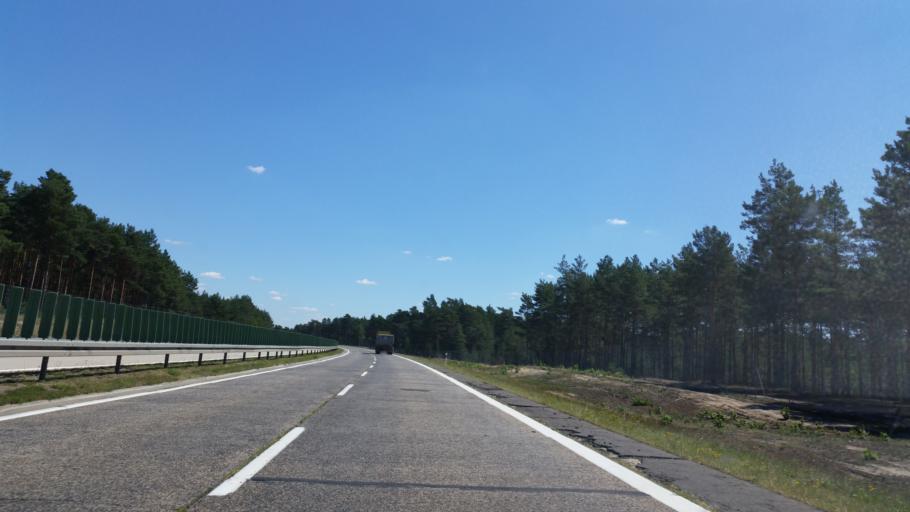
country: PL
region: Lubusz
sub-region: Powiat zaganski
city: Malomice
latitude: 51.4328
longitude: 15.3743
